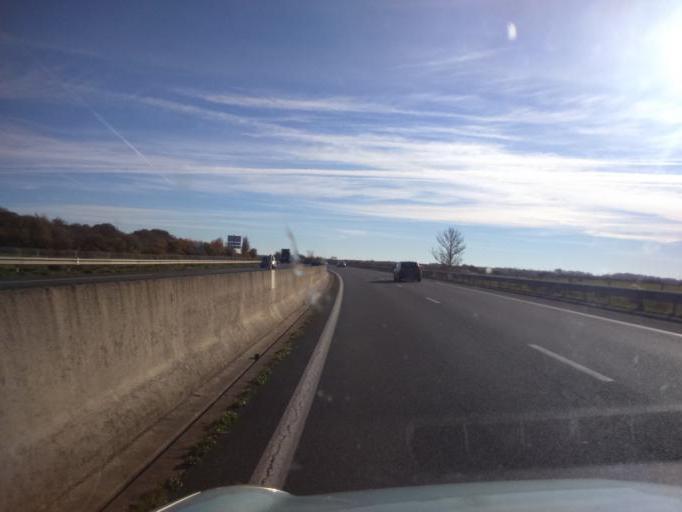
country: FR
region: Poitou-Charentes
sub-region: Departement de la Charente-Maritime
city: Saint-Laurent-de-la-Pree
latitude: 45.9810
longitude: -1.0133
